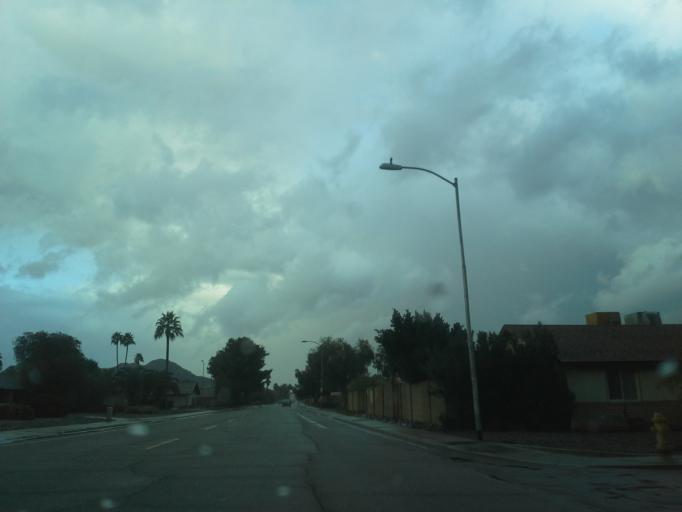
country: US
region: Arizona
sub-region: Maricopa County
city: Paradise Valley
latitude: 33.5903
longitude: -112.0218
